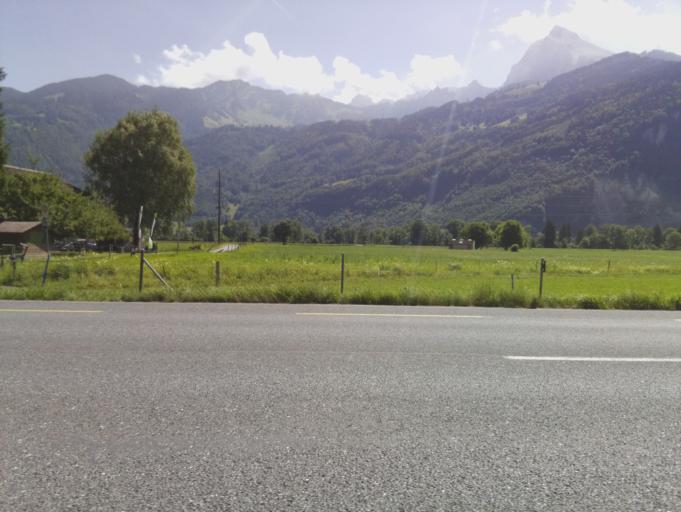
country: CH
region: Glarus
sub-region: Glarus
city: Nafels
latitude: 47.0833
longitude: 9.0551
